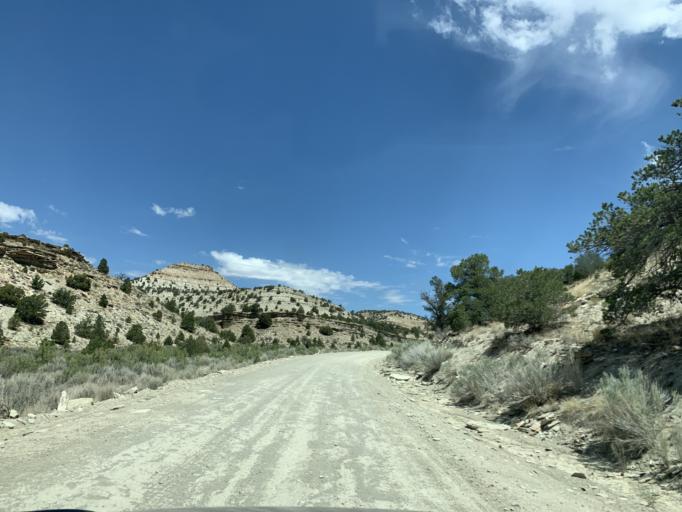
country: US
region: Utah
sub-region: Duchesne County
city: Duchesne
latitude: 39.8587
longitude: -110.2527
